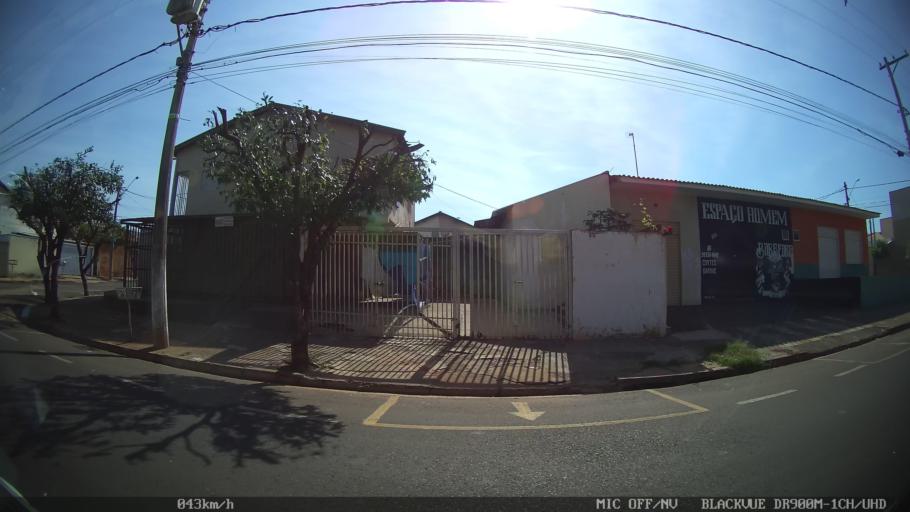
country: BR
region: Sao Paulo
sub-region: Sao Jose Do Rio Preto
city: Sao Jose do Rio Preto
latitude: -20.7919
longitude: -49.4403
